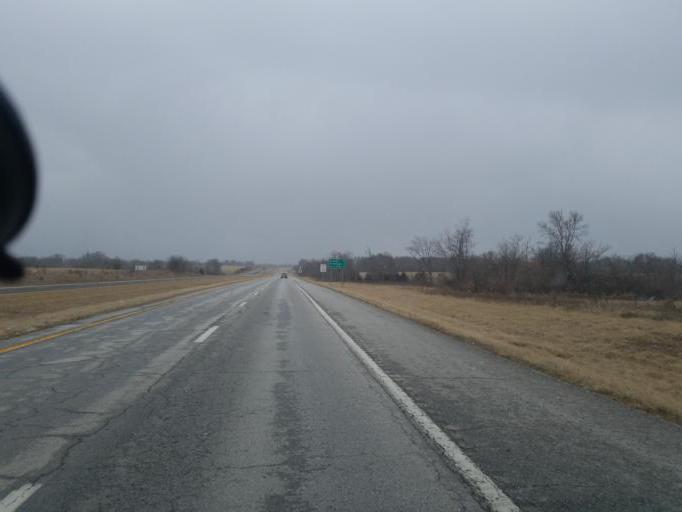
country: US
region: Missouri
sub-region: Macon County
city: La Plata
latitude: 39.8976
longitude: -92.4720
